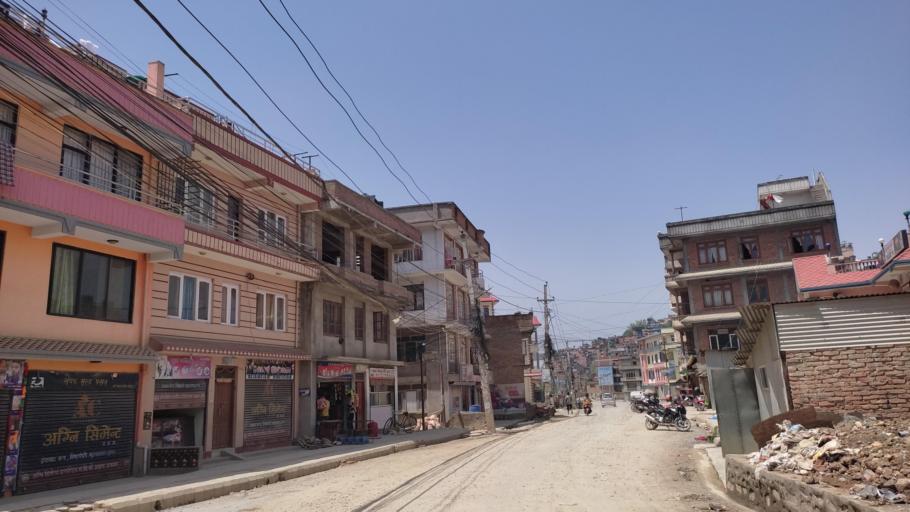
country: NP
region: Central Region
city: Kirtipur
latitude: 27.6749
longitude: 85.2727
